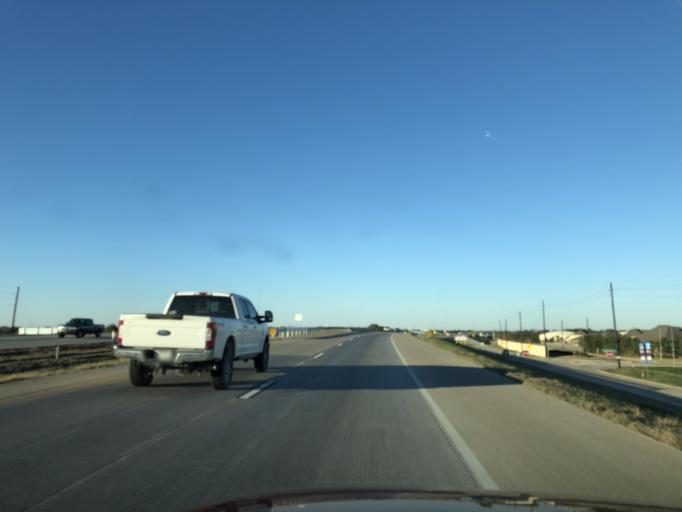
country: US
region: Texas
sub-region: Harris County
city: Cypress
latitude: 30.0137
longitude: -95.7690
